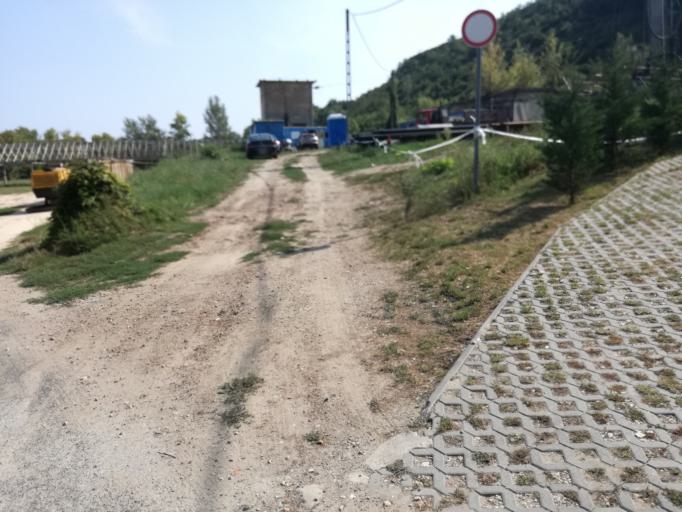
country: HU
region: Pest
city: Szazhalombatta
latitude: 47.3504
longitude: 18.9418
